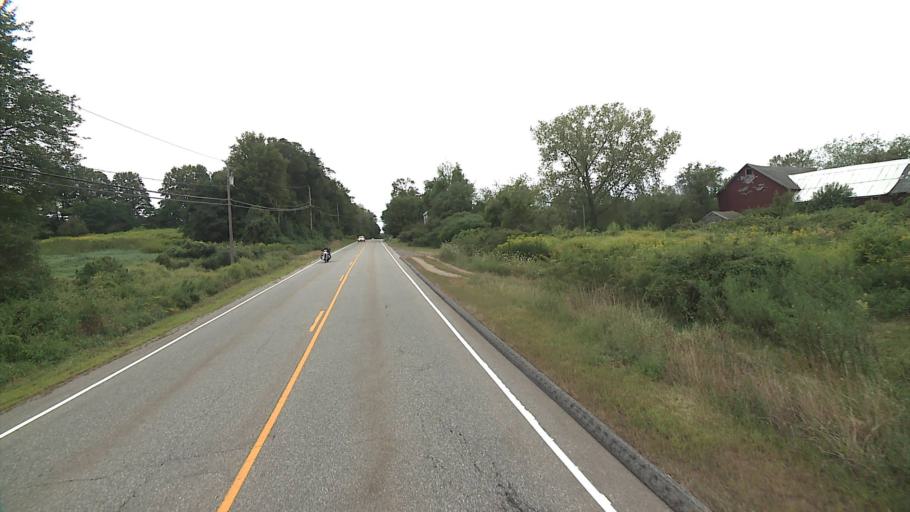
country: US
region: Connecticut
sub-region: Hartford County
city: Terramuggus
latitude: 41.7089
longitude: -72.4330
